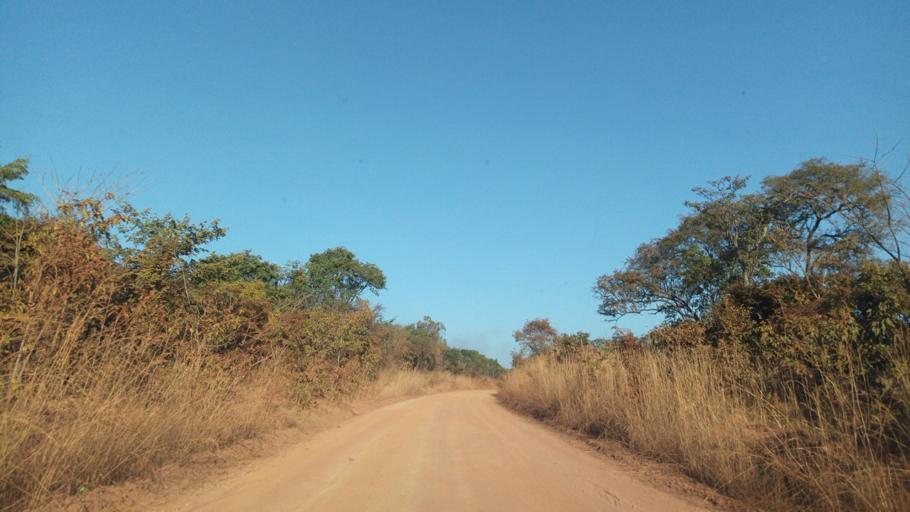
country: ZM
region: Luapula
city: Mwense
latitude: -10.4851
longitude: 28.4974
